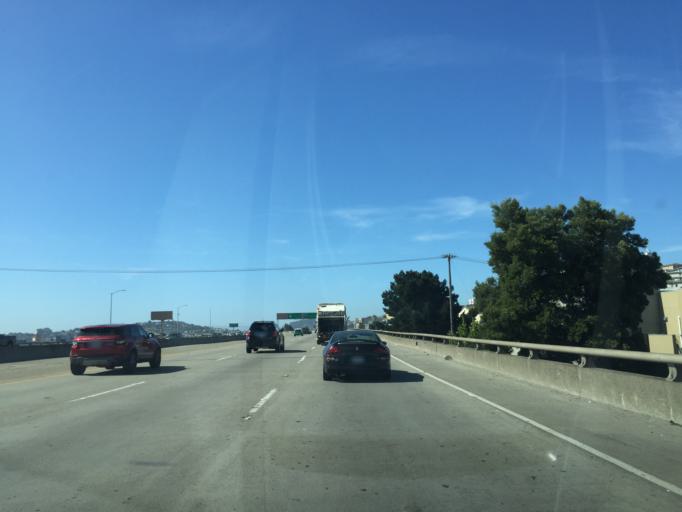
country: US
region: California
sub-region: San Francisco County
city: San Francisco
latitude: 37.7585
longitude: -122.3926
